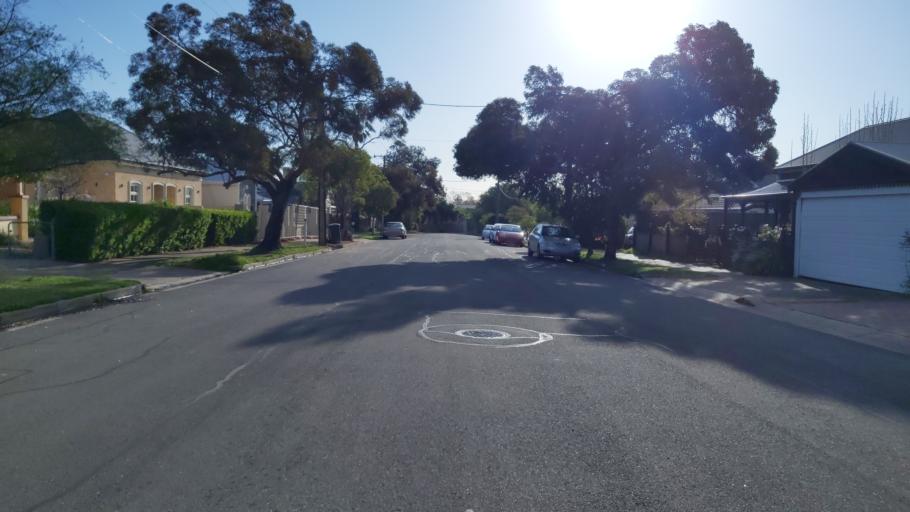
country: AU
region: South Australia
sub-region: Unley
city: Fullarton
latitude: -34.9516
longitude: 138.6301
